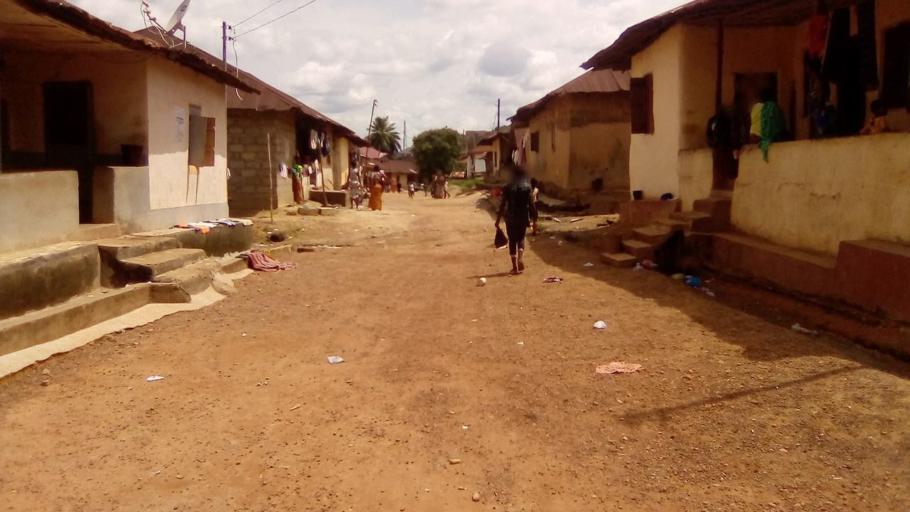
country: SL
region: Southern Province
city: Bo
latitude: 7.9664
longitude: -11.7341
